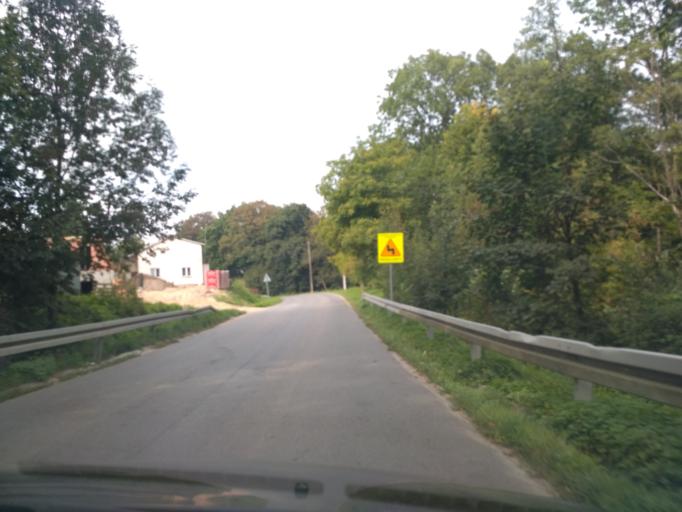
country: PL
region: Subcarpathian Voivodeship
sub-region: Powiat rzeszowski
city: Trzciana
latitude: 50.0530
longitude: 21.8325
